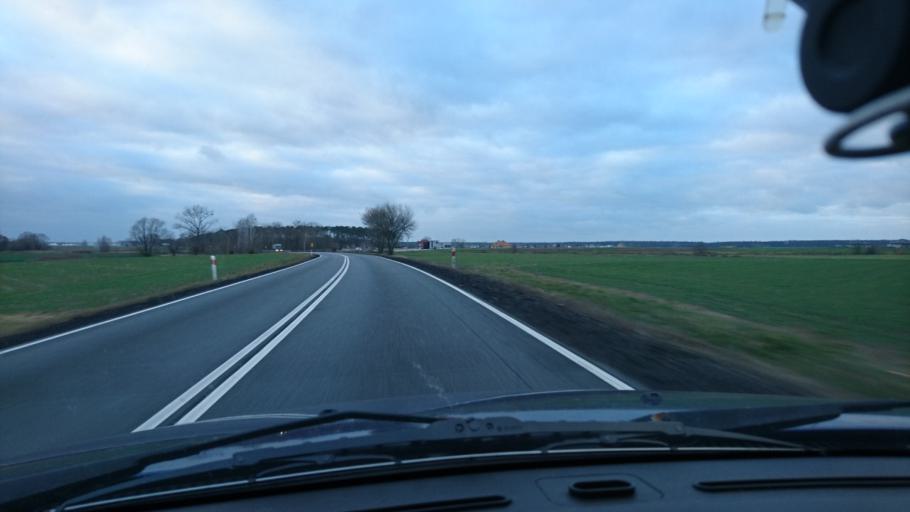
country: PL
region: Greater Poland Voivodeship
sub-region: Powiat kepinski
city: Opatow
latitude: 51.2200
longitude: 18.1358
